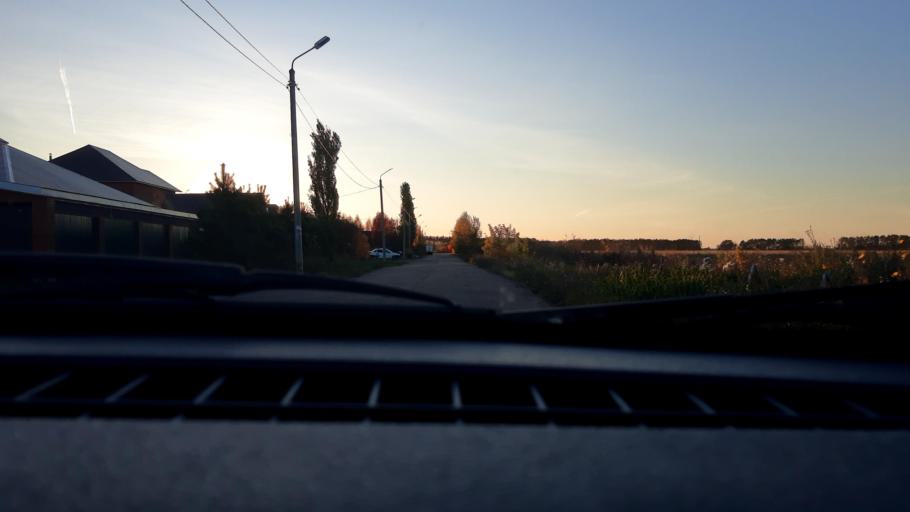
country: RU
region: Bashkortostan
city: Ufa
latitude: 54.8585
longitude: 56.0199
